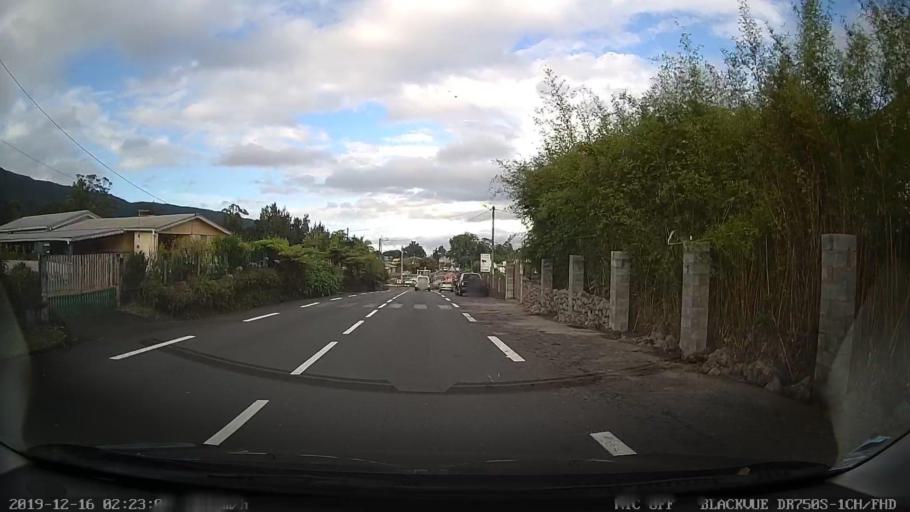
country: RE
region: Reunion
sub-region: Reunion
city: Salazie
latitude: -21.1444
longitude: 55.6195
